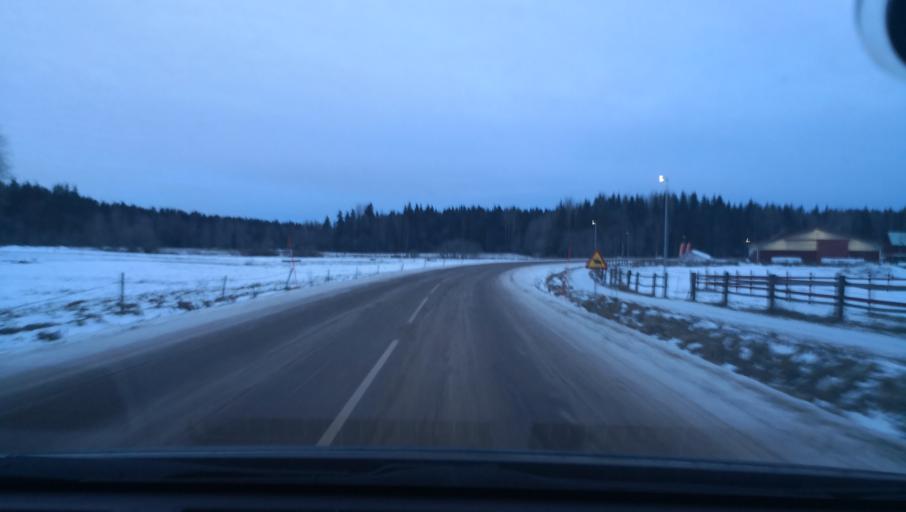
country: SE
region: Dalarna
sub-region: Avesta Kommun
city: Horndal
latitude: 60.1976
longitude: 16.4623
